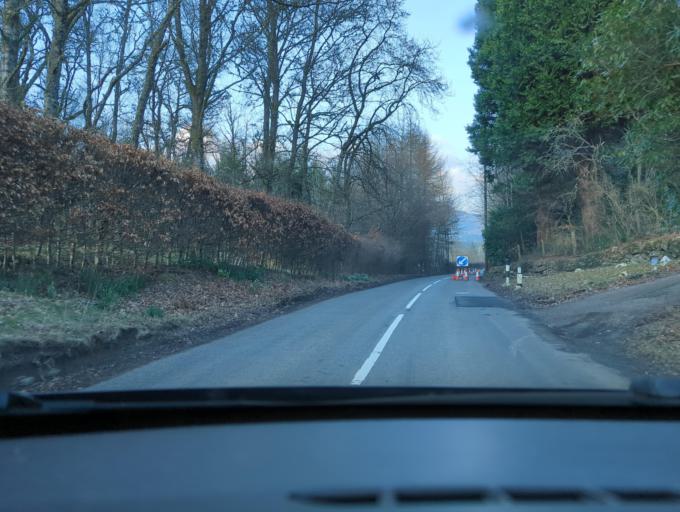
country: GB
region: Scotland
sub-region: Perth and Kinross
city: Methven
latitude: 56.5399
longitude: -3.6633
